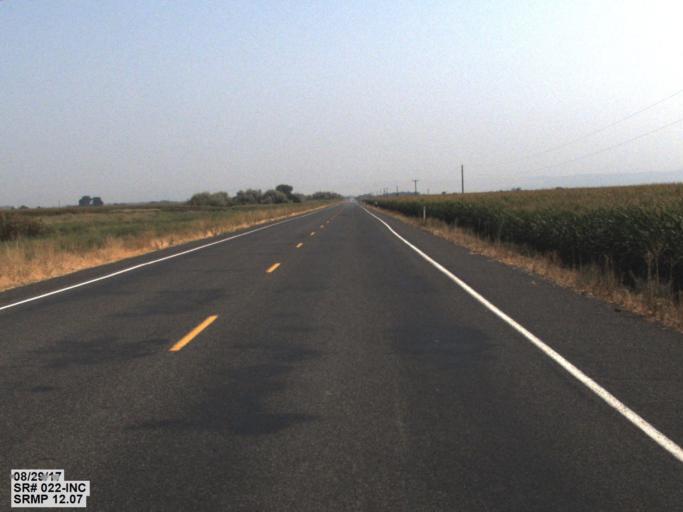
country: US
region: Washington
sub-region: Yakima County
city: Granger
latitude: 46.2969
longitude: -120.1900
